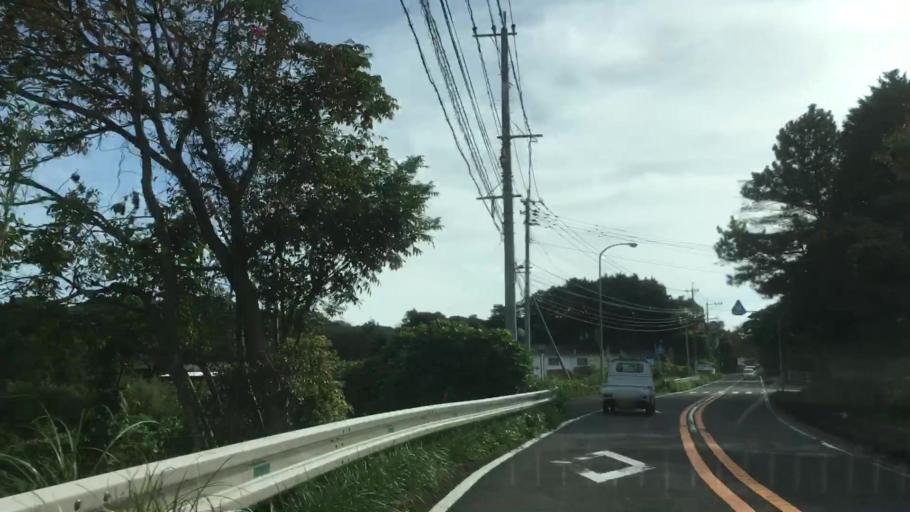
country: JP
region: Nagasaki
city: Sasebo
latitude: 33.0308
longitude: 129.6567
